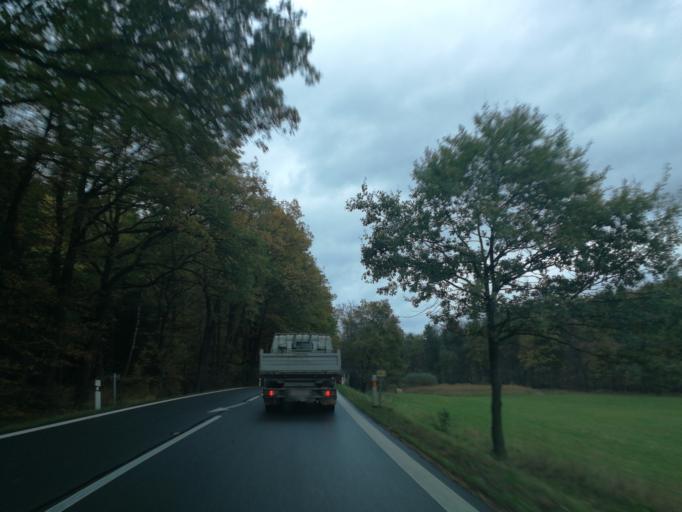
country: CZ
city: Hodslavice
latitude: 49.5063
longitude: 17.9976
